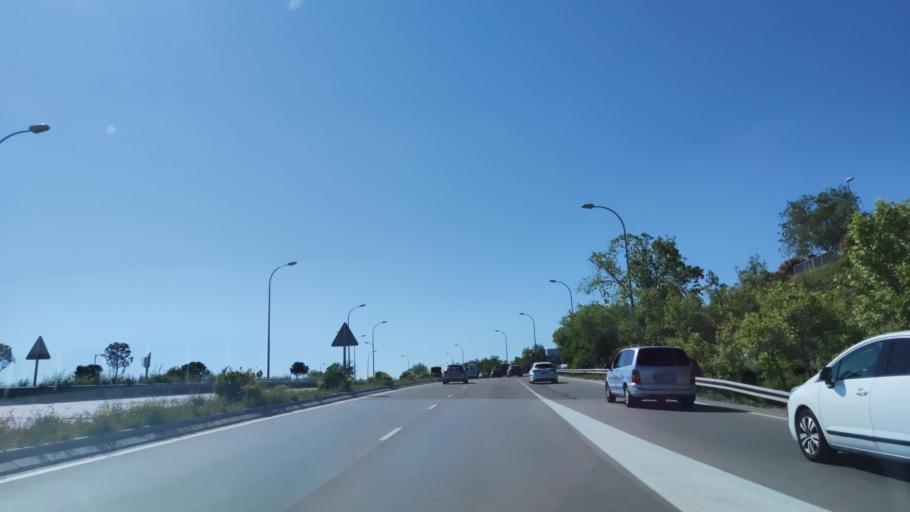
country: ES
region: Madrid
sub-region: Provincia de Madrid
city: San Blas
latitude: 40.4323
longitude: -3.5998
